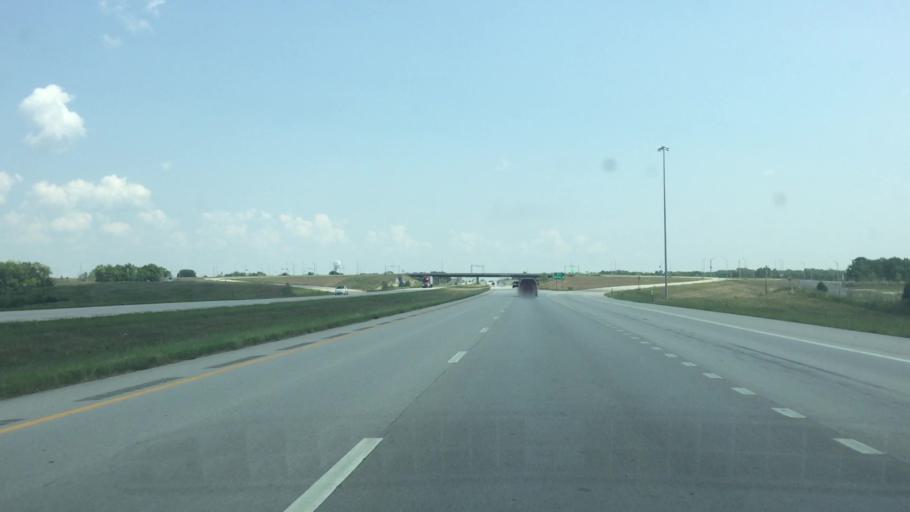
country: US
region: Kansas
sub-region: Johnson County
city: Edgerton
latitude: 38.7557
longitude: -94.9706
